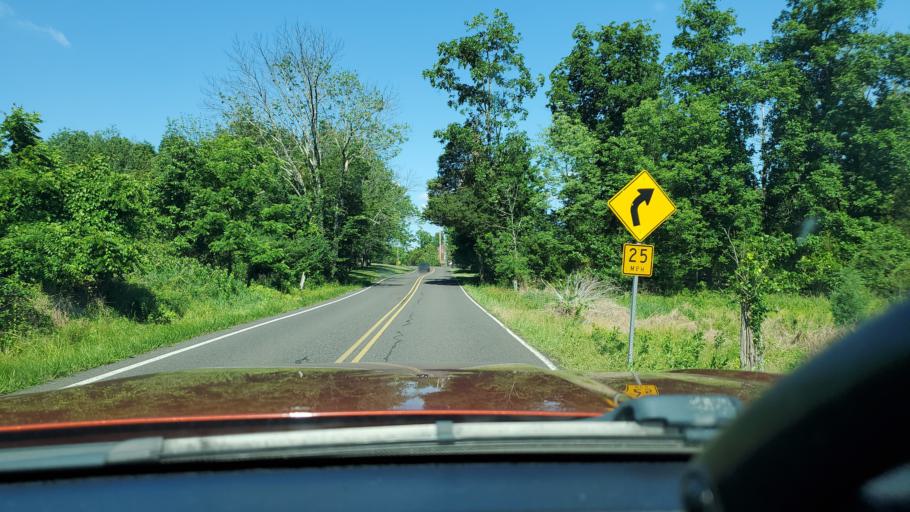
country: US
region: Pennsylvania
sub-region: Montgomery County
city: Red Hill
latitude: 40.3549
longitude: -75.4924
